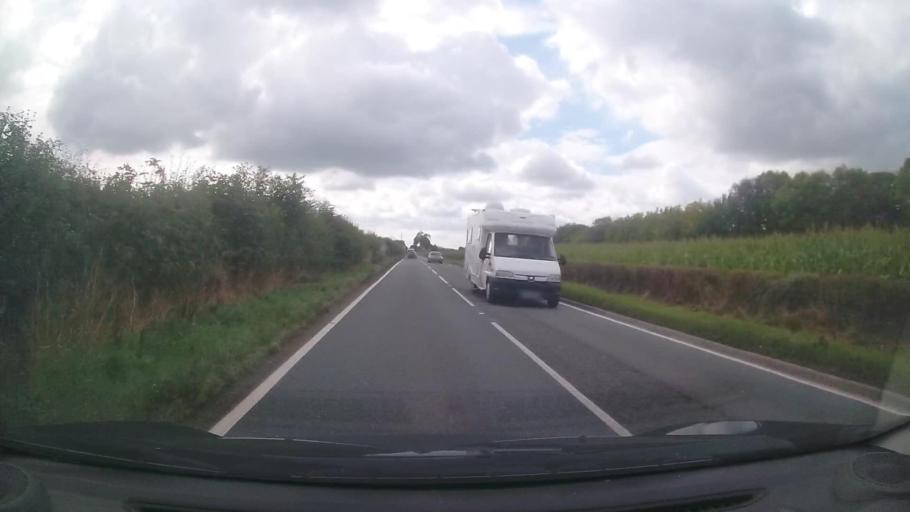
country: GB
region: England
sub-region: Shropshire
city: Pant
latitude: 52.7510
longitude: -3.0904
